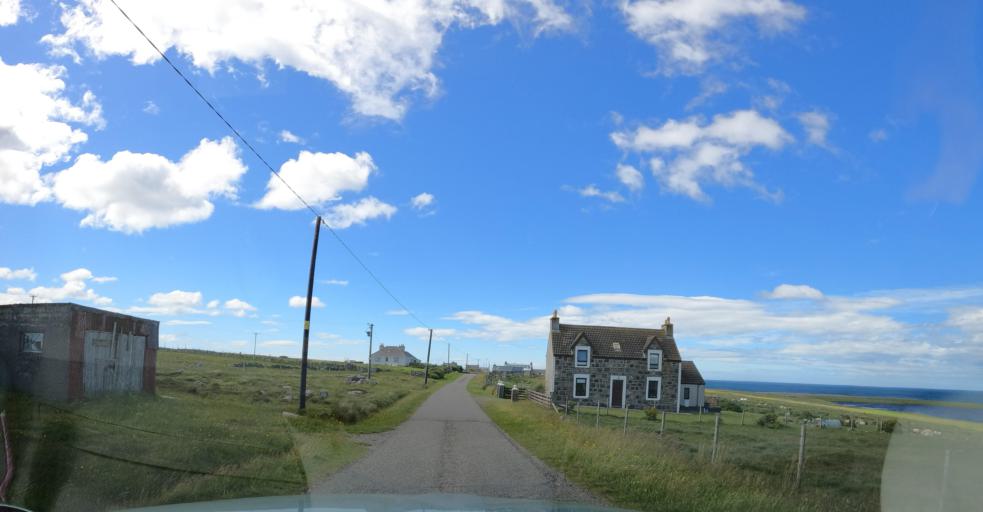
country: GB
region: Scotland
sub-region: Eilean Siar
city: Isle of Lewis
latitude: 58.3563
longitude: -6.5545
